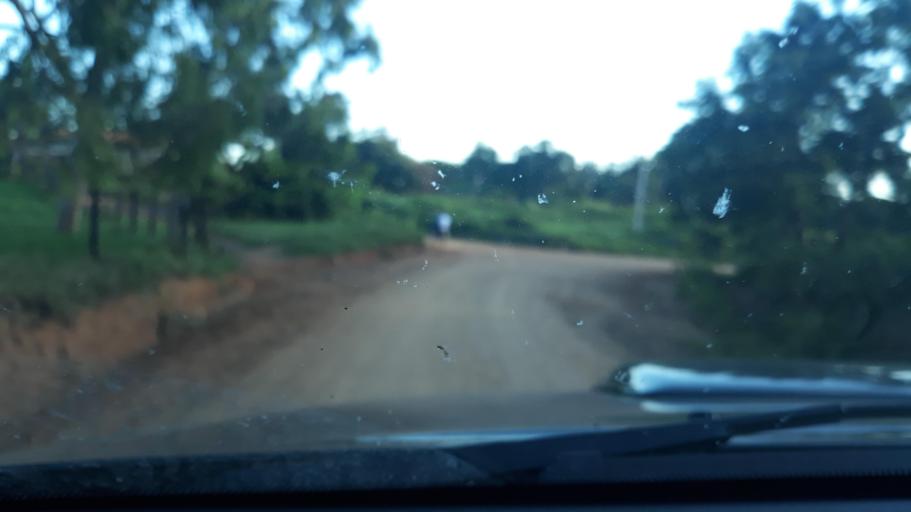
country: BR
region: Bahia
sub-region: Riacho De Santana
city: Riacho de Santana
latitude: -13.8275
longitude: -42.7275
